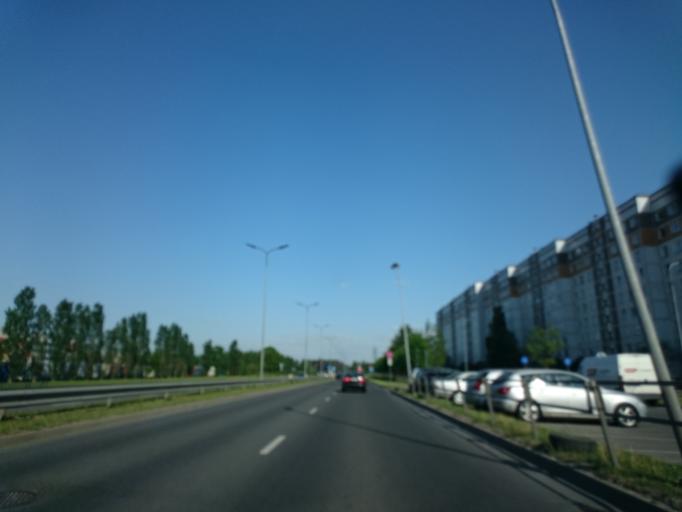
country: LV
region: Stopini
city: Ulbroka
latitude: 56.9441
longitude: 24.2235
